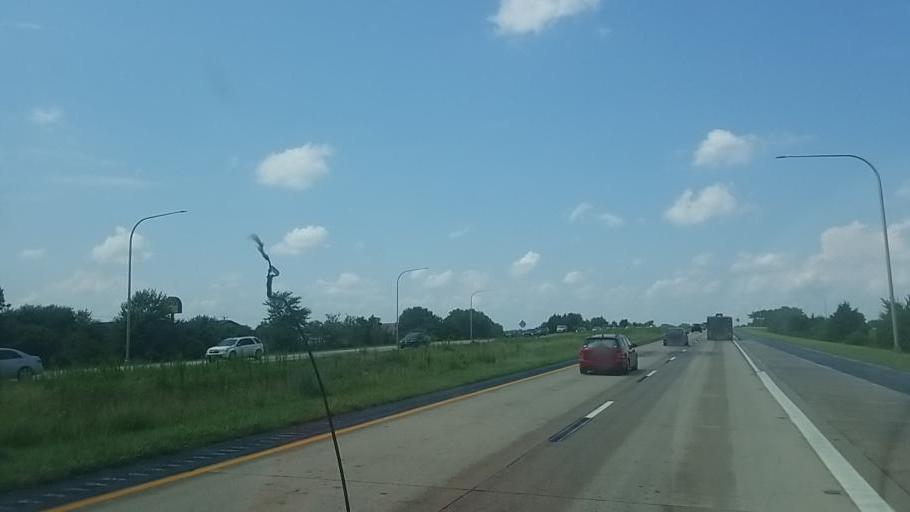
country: US
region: Delaware
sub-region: Kent County
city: Smyrna
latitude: 39.2787
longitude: -75.5866
